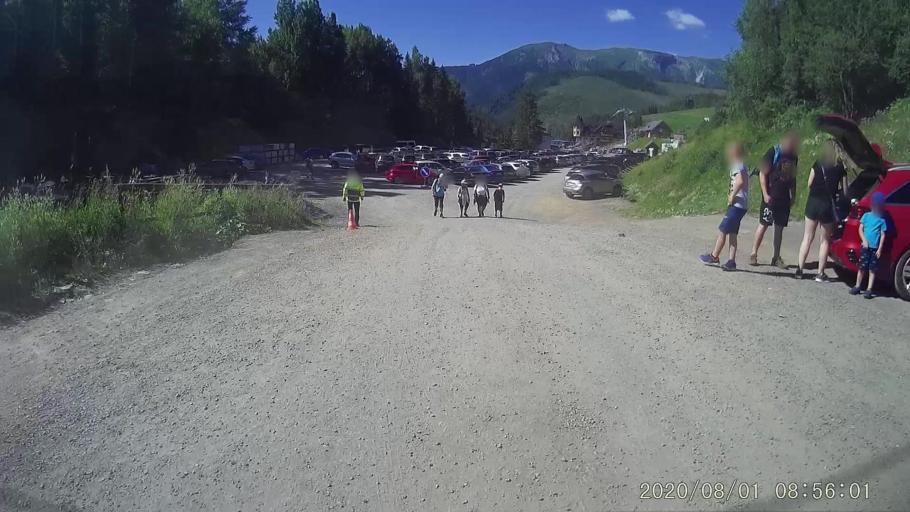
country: SK
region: Presovsky
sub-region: Okres Poprad
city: Zdiar
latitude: 49.2740
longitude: 20.3120
